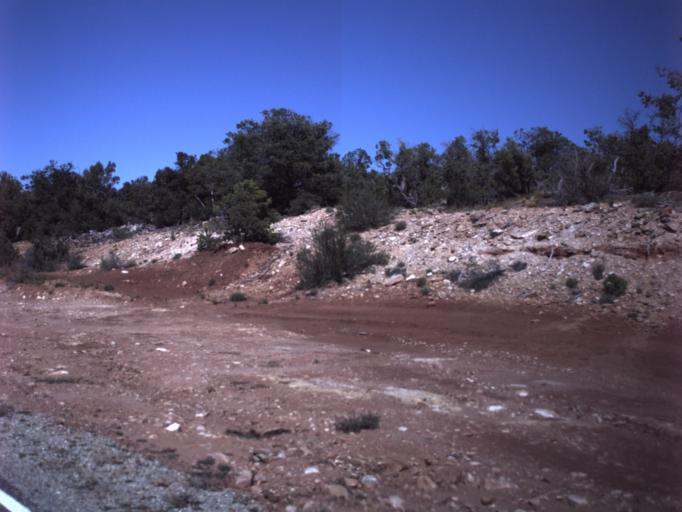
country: US
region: Utah
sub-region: San Juan County
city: Blanding
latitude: 37.5462
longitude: -109.8898
